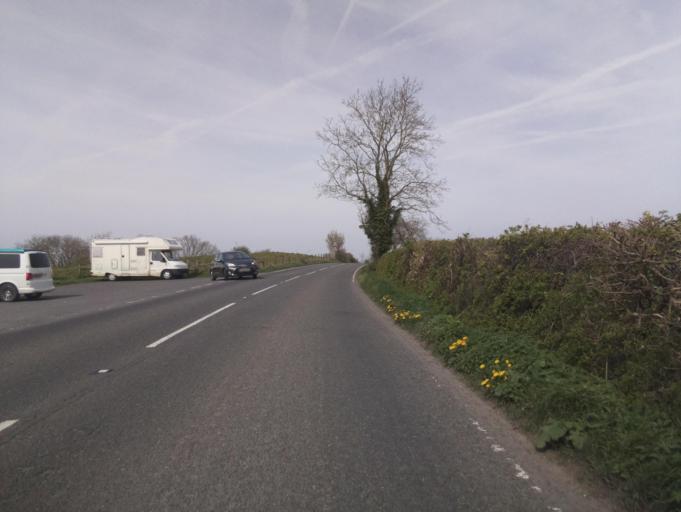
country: GB
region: England
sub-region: Somerset
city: Street
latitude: 51.1123
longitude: -2.7635
